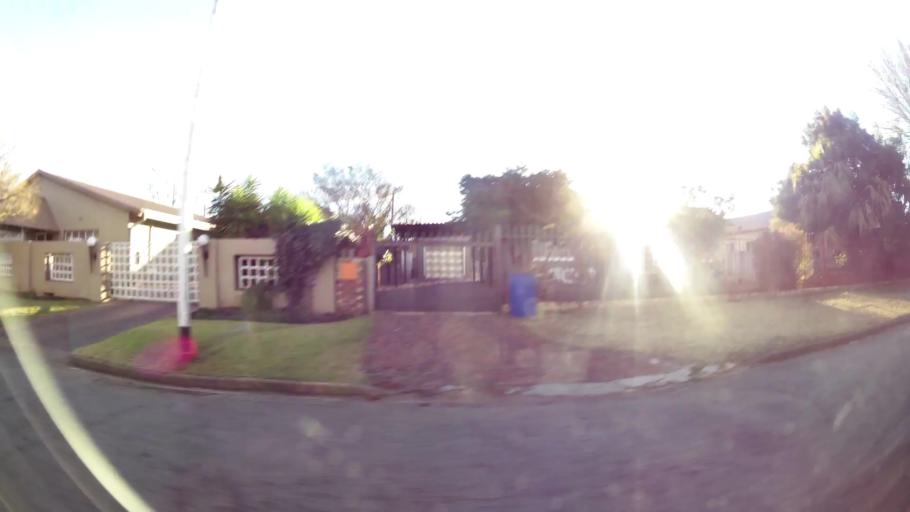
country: ZA
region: North-West
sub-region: Dr Kenneth Kaunda District Municipality
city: Potchefstroom
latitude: -26.7265
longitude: 27.1001
